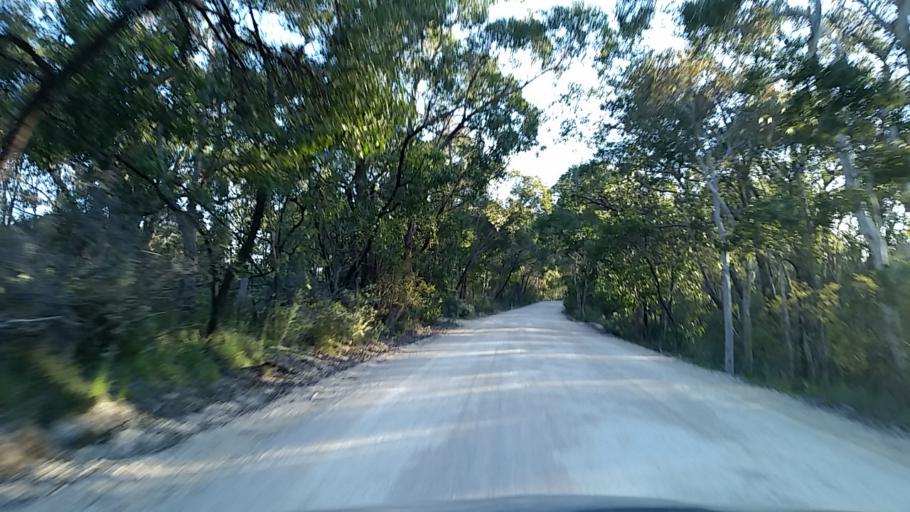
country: AU
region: South Australia
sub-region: Alexandrina
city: Mount Compass
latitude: -35.2992
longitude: 138.6821
